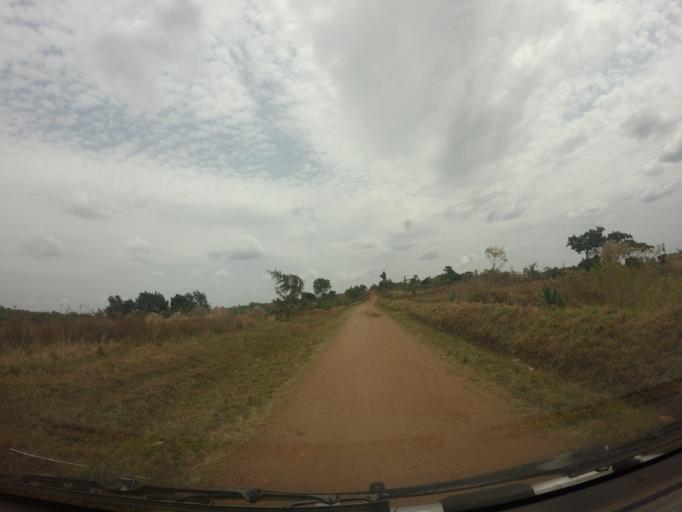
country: UG
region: Northern Region
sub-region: Arua District
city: Arua
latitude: 2.8224
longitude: 30.9031
